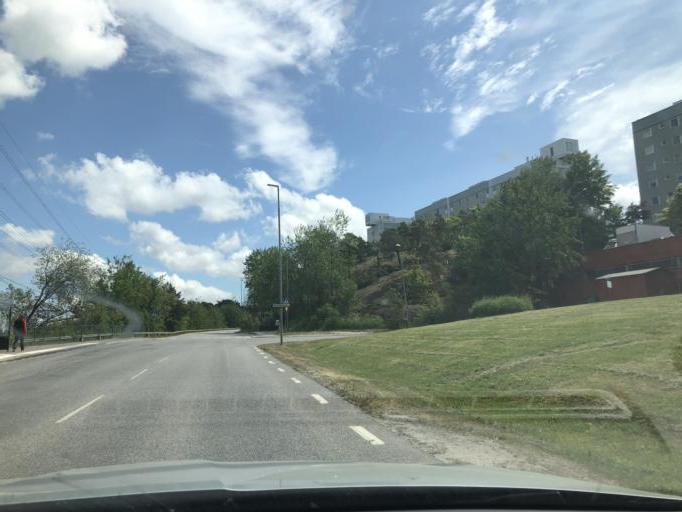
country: SE
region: Stockholm
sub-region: Botkyrka Kommun
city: Alby
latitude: 59.2432
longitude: 17.8492
